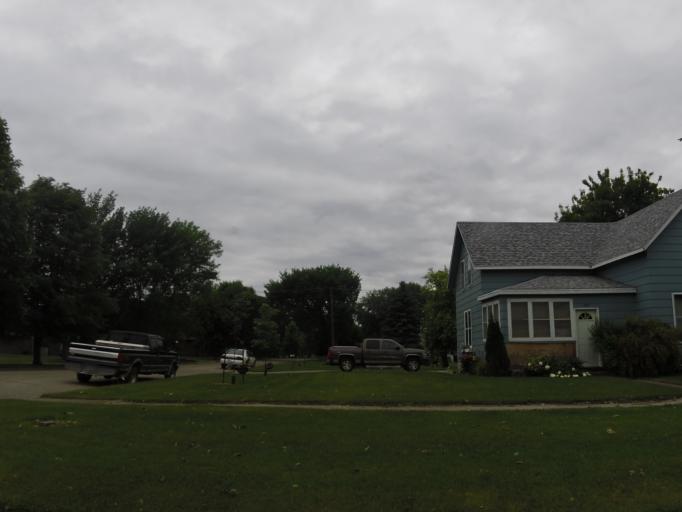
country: US
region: North Dakota
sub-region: Walsh County
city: Grafton
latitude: 48.6172
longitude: -97.4506
